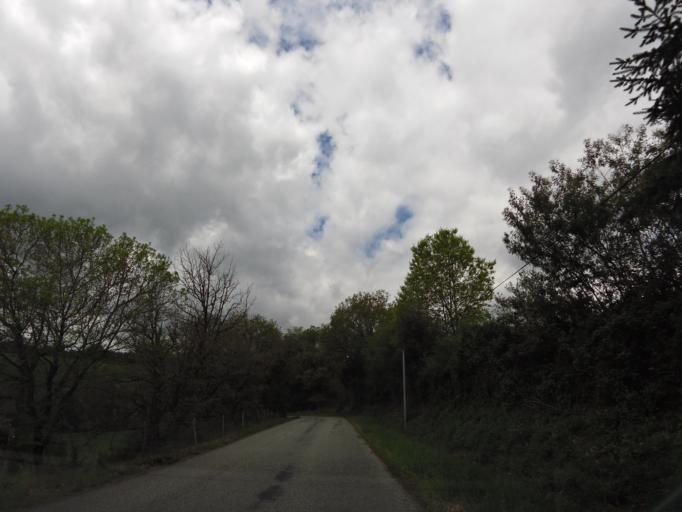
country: FR
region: Languedoc-Roussillon
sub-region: Departement de l'Aude
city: Villepinte
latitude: 43.3500
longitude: 2.0794
